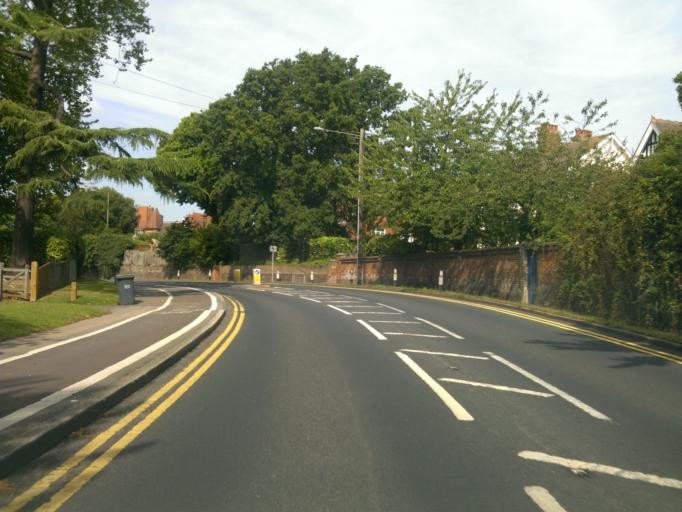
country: GB
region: England
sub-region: Kent
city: Tonbridge
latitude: 51.2030
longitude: 0.2731
